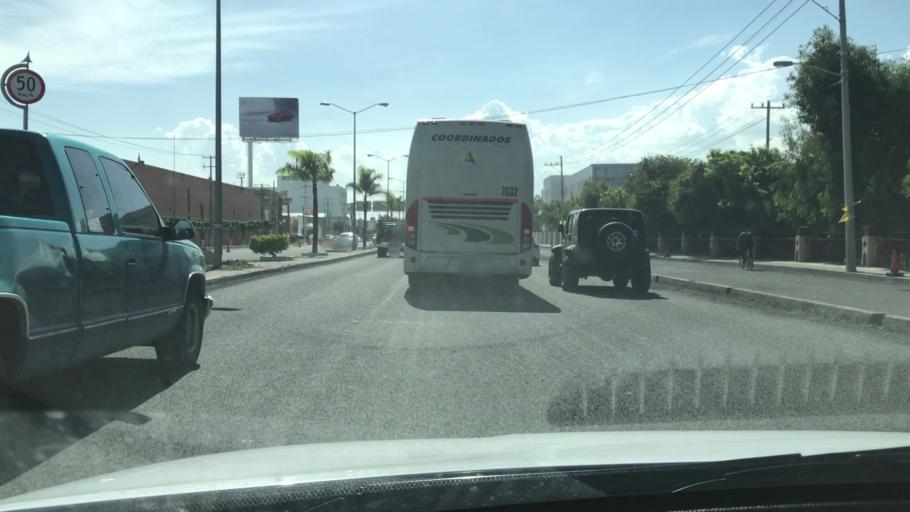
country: MX
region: Guanajuato
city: Celaya
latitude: 20.5162
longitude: -100.7833
